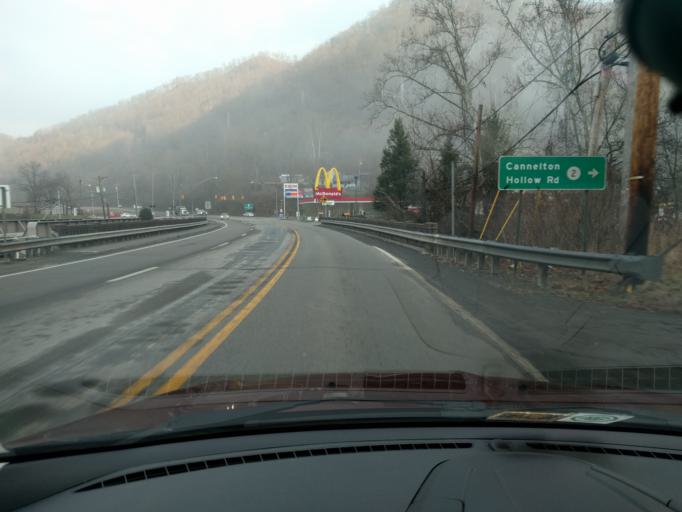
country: US
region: West Virginia
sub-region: Kanawha County
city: Montgomery
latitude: 38.1808
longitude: -81.3065
